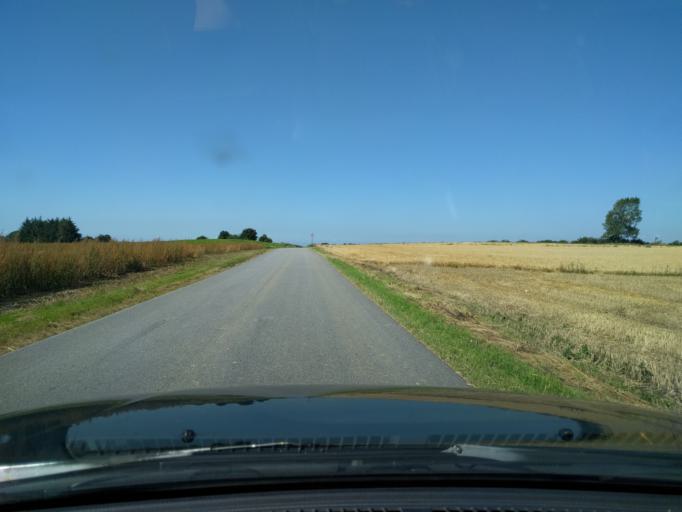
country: DK
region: Zealand
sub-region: Vordingborg Kommune
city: Orslev
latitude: 55.0867
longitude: 11.9358
